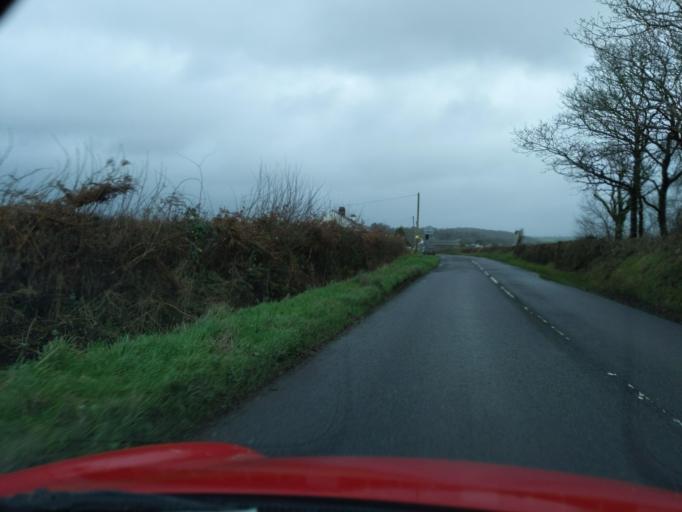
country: GB
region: England
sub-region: Cornwall
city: Werrington
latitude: 50.6830
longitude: -4.3239
